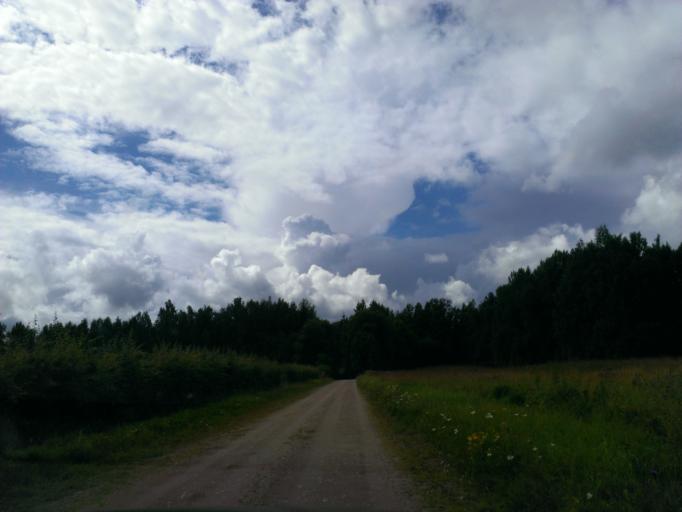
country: LV
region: Ligatne
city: Ligatne
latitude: 57.2250
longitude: 24.9873
